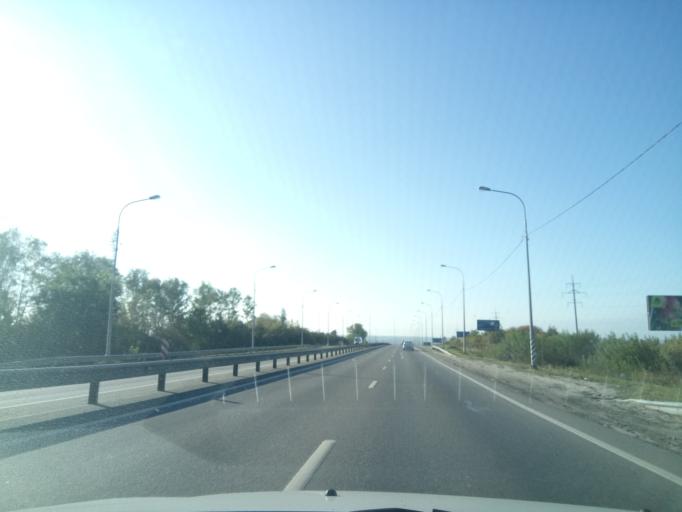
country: RU
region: Nizjnij Novgorod
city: Burevestnik
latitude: 56.1967
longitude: 43.9247
